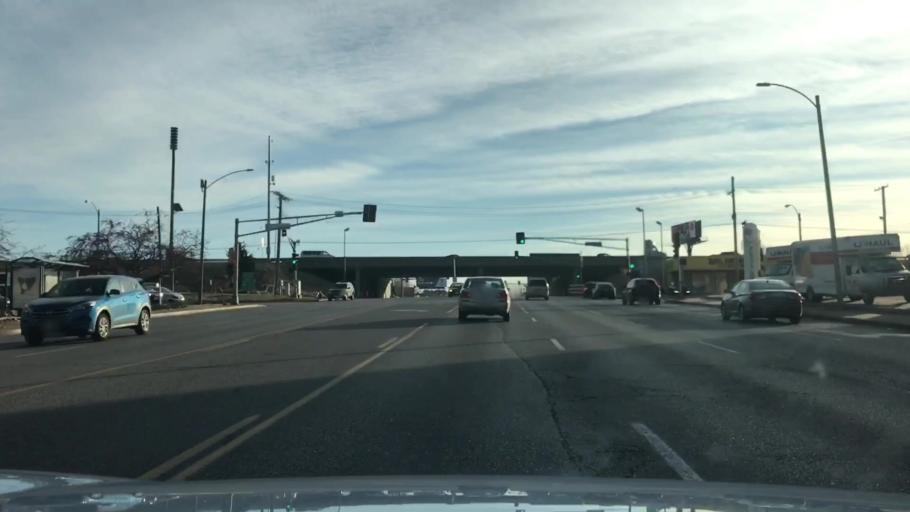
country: US
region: Missouri
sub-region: Saint Louis County
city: Richmond Heights
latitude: 38.6198
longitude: -90.2663
